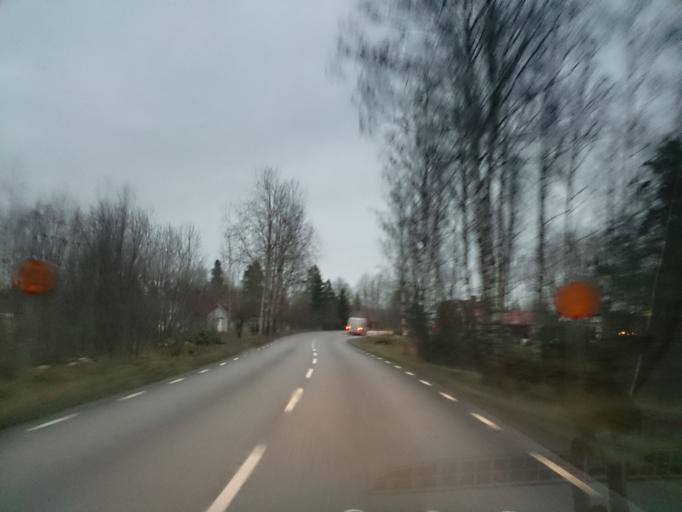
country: SE
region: OEstergoetland
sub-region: Linkopings Kommun
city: Linghem
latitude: 58.4114
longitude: 15.7626
